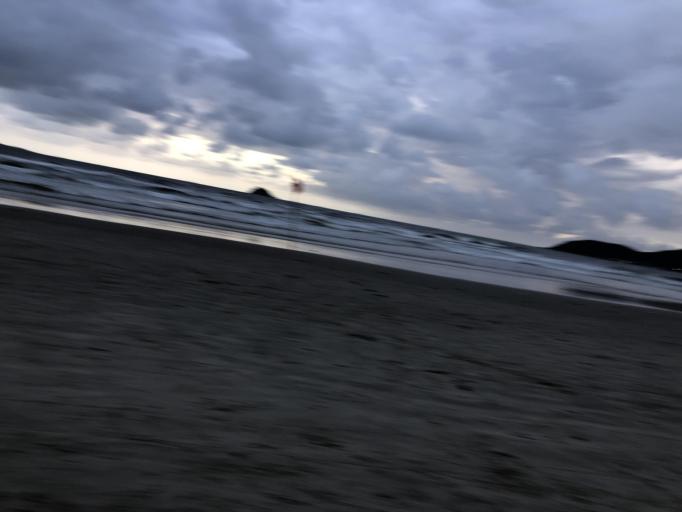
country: BR
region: Santa Catarina
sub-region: Sao Francisco Do Sul
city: Sao Francisco do Sul
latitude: -26.2133
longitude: -48.5236
